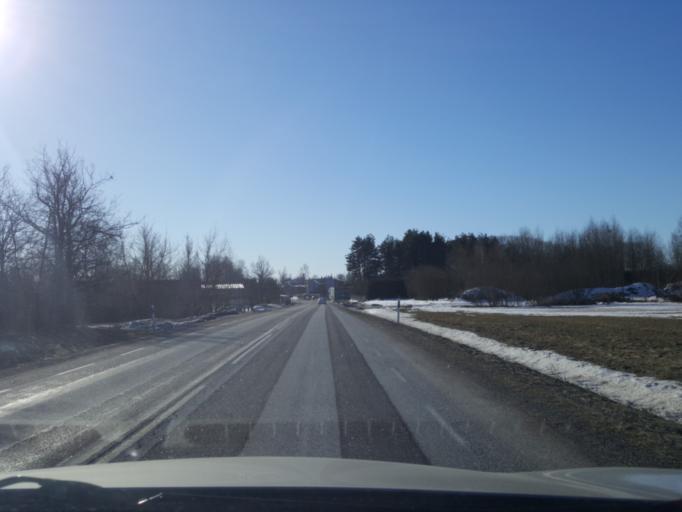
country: EE
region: Viljandimaa
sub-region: Viljandi linn
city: Viljandi
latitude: 58.3807
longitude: 25.6037
